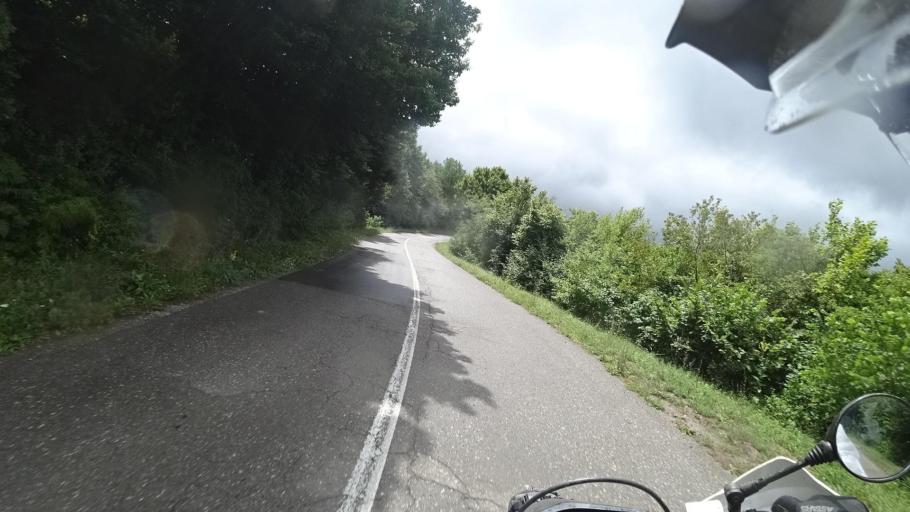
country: HR
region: Karlovacka
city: Plaski
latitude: 45.0290
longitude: 15.4150
